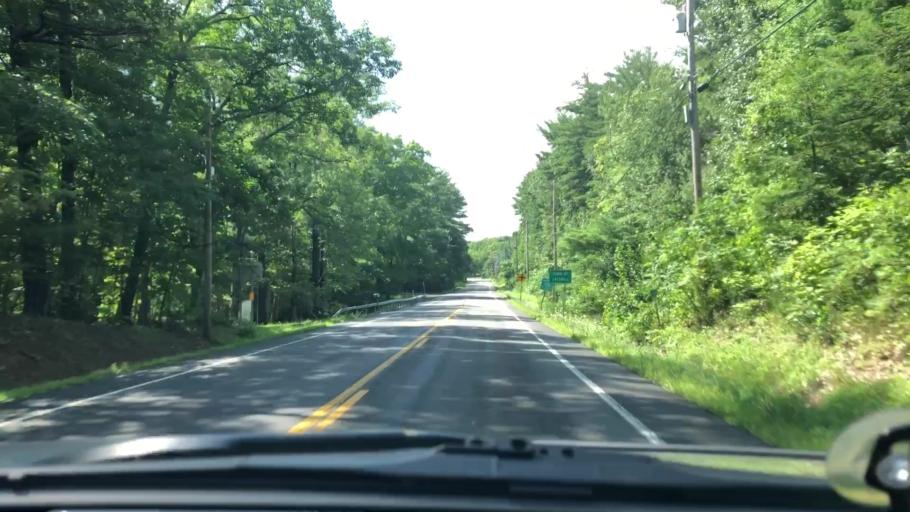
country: US
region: New York
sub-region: Greene County
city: Cairo
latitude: 42.2592
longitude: -73.9770
